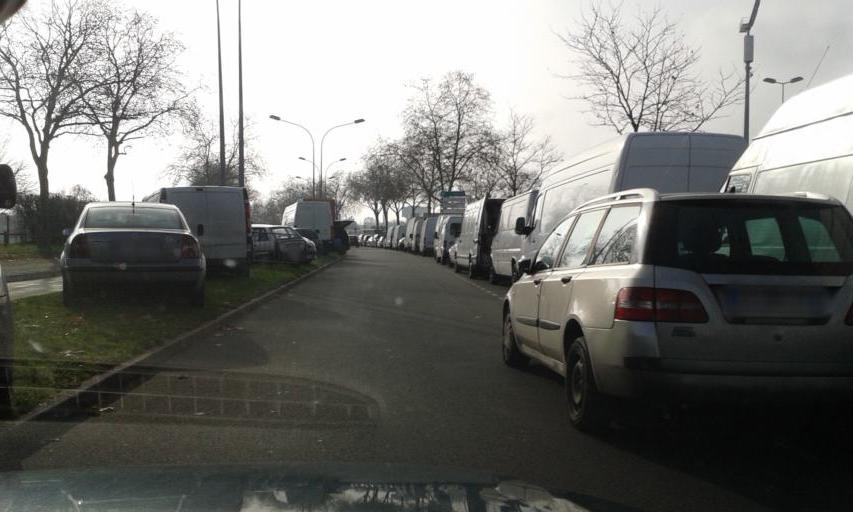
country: FR
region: Centre
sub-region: Departement du Loiret
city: Saint-Cyr-en-Val
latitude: 47.8410
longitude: 1.9438
